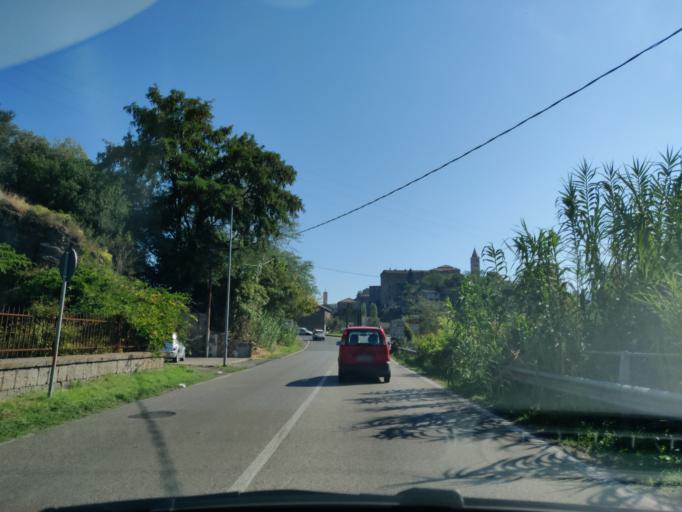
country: IT
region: Latium
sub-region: Provincia di Viterbo
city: Viterbo
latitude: 42.4151
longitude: 12.0959
